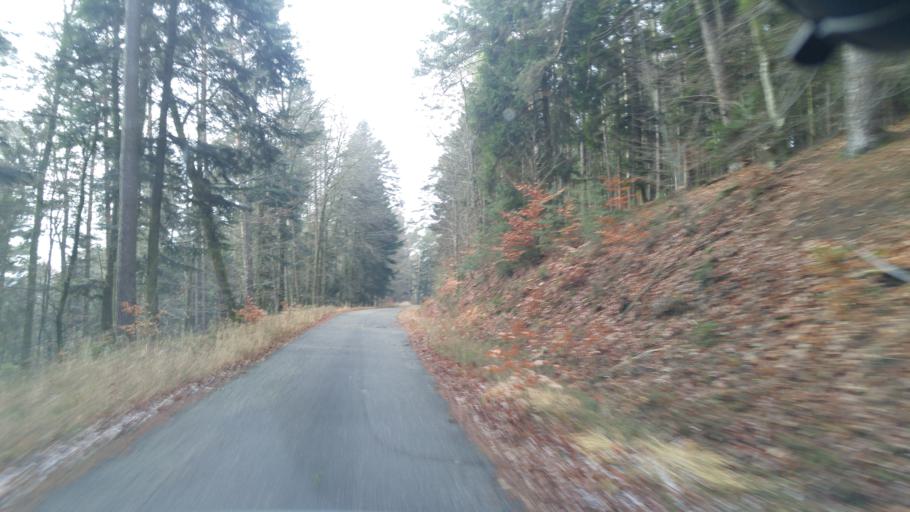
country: DE
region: Rheinland-Pfalz
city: Bollenborn
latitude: 49.1056
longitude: 7.9099
